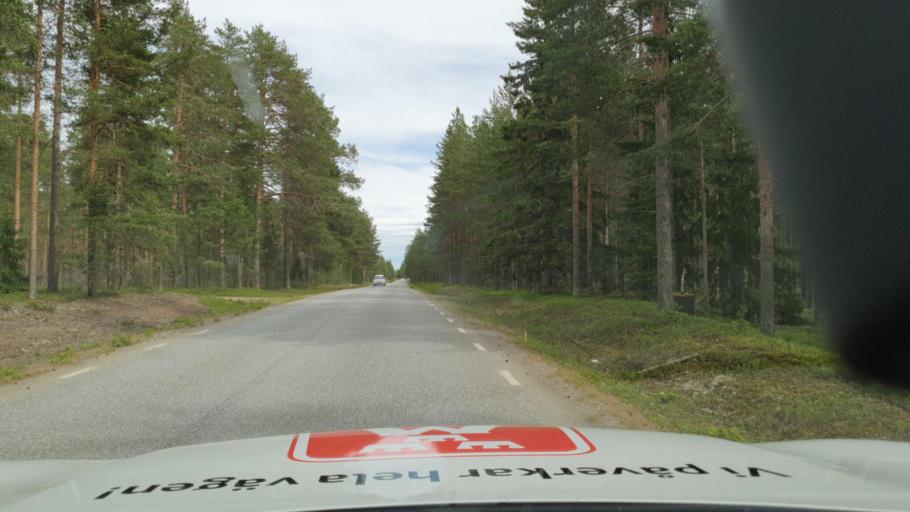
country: SE
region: Vaesterbotten
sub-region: Skelleftea Kommun
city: Burtraesk
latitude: 64.5050
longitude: 20.7735
